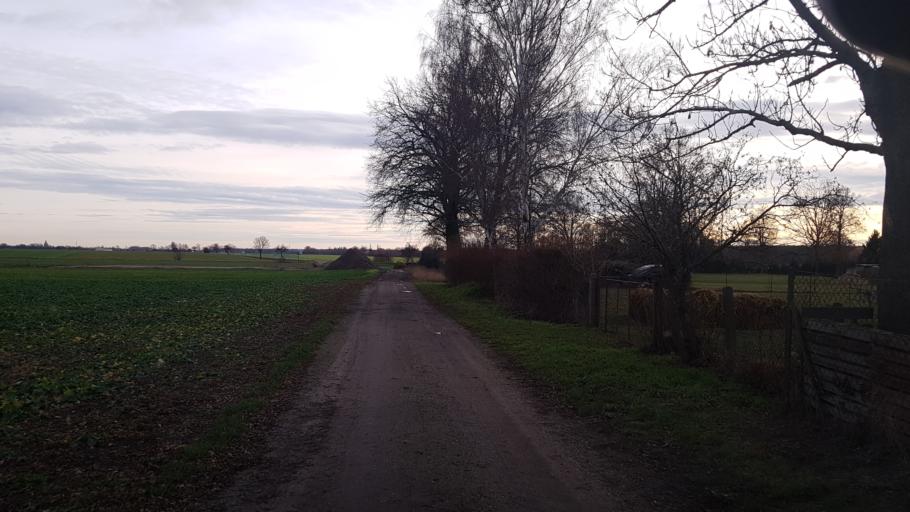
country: DE
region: Brandenburg
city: Doberlug-Kirchhain
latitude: 51.6712
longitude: 13.5131
